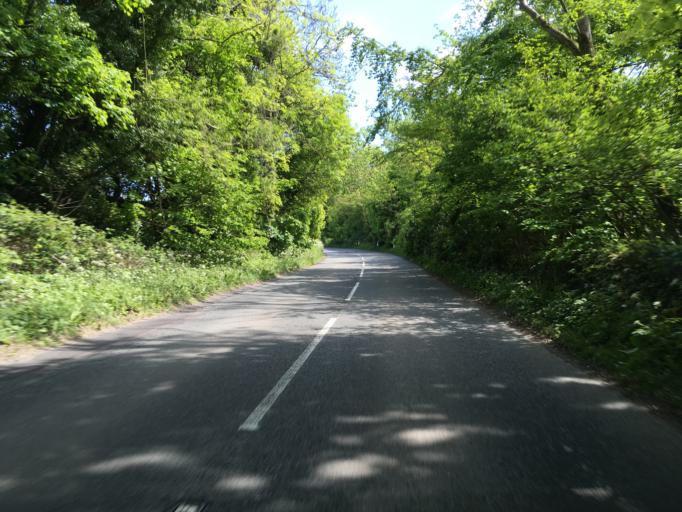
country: GB
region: England
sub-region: Gloucestershire
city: Dursley
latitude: 51.6691
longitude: -2.3150
